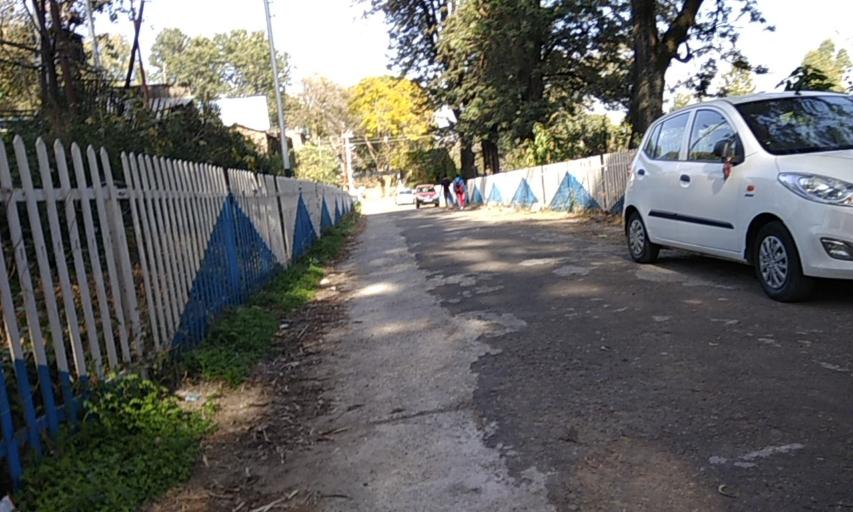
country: IN
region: Himachal Pradesh
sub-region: Kangra
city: Palampur
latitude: 32.0831
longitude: 76.5158
